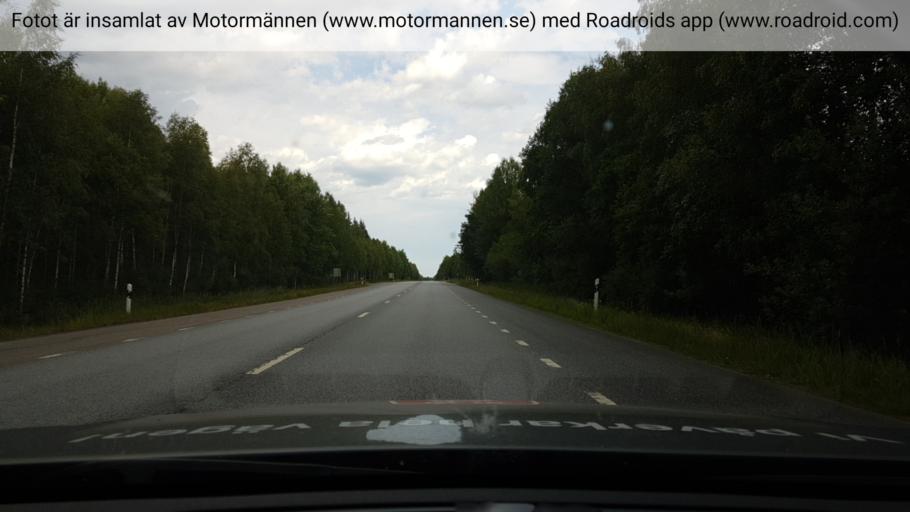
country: SE
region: Uppsala
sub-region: Heby Kommun
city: Morgongava
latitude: 59.8960
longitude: 17.1182
